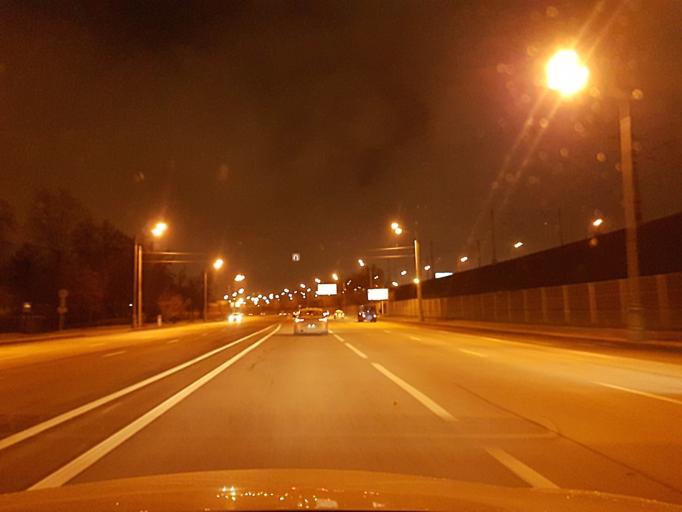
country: RU
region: Moscow
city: Luzhniki
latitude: 55.7263
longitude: 37.5501
